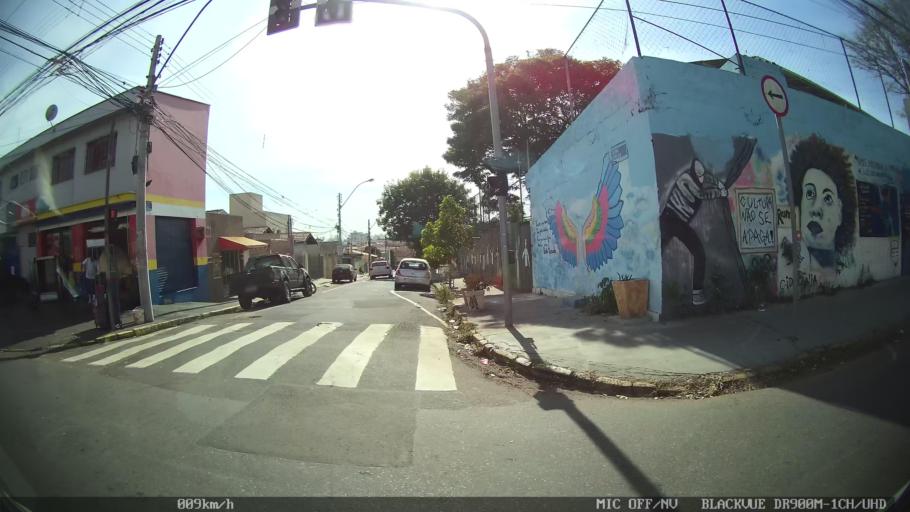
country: BR
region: Sao Paulo
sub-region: Piracicaba
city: Piracicaba
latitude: -22.7517
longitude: -47.6510
